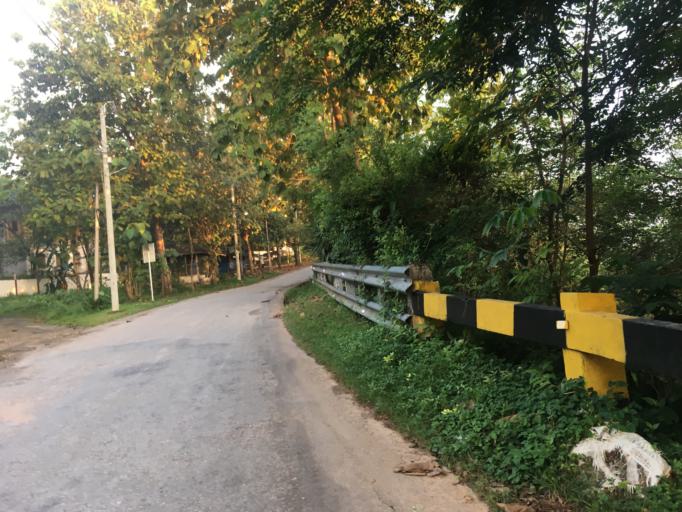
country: MM
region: Mon
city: Mawlamyine
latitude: 16.4718
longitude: 97.6306
